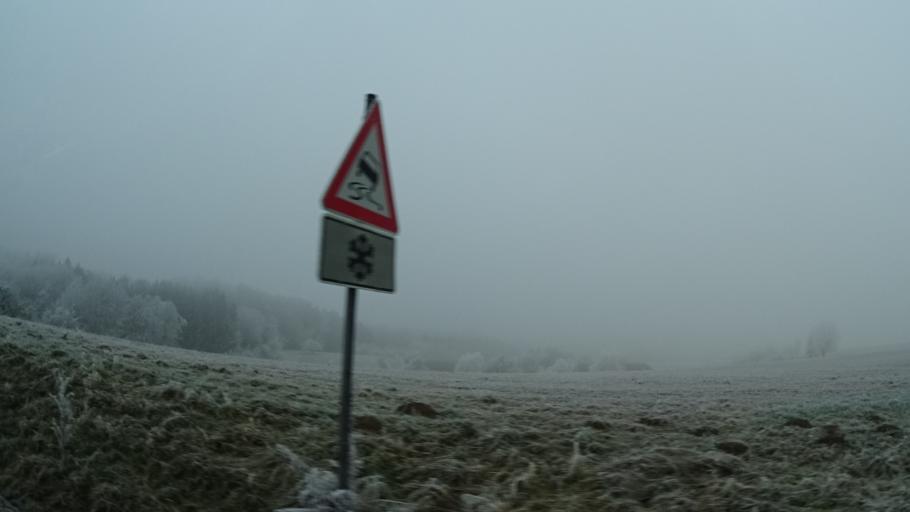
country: DE
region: Bavaria
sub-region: Regierungsbezirk Unterfranken
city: Hosbach
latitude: 50.0326
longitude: 9.1973
